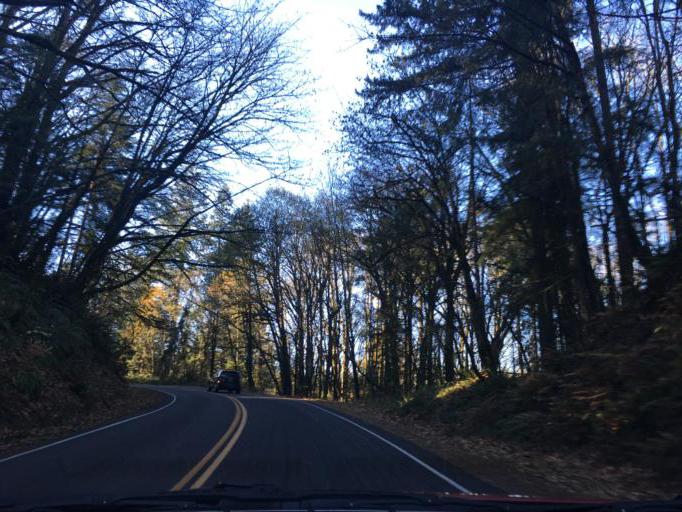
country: US
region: Oregon
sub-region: Washington County
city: Cedar Mill
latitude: 45.5899
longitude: -122.7909
